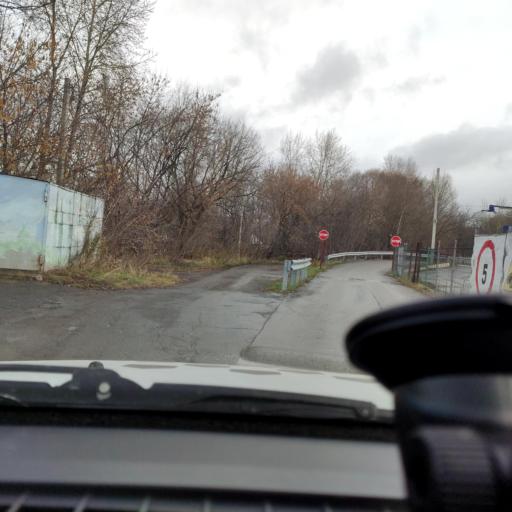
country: RU
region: Perm
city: Perm
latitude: 58.0296
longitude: 56.2955
